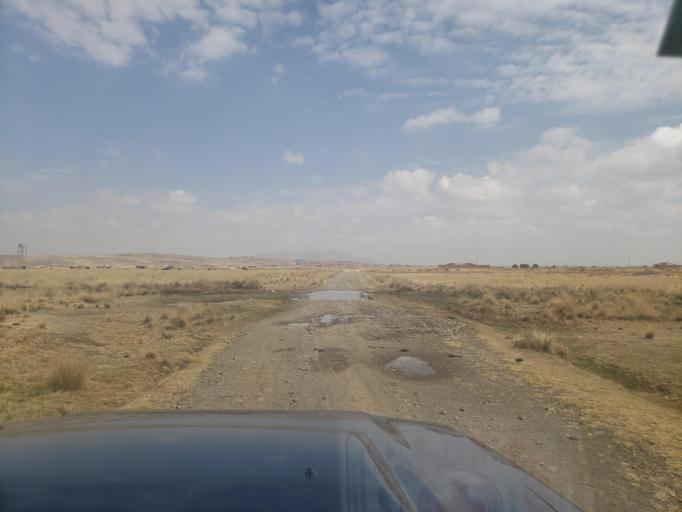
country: BO
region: La Paz
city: Batallas
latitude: -16.4084
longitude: -68.4479
